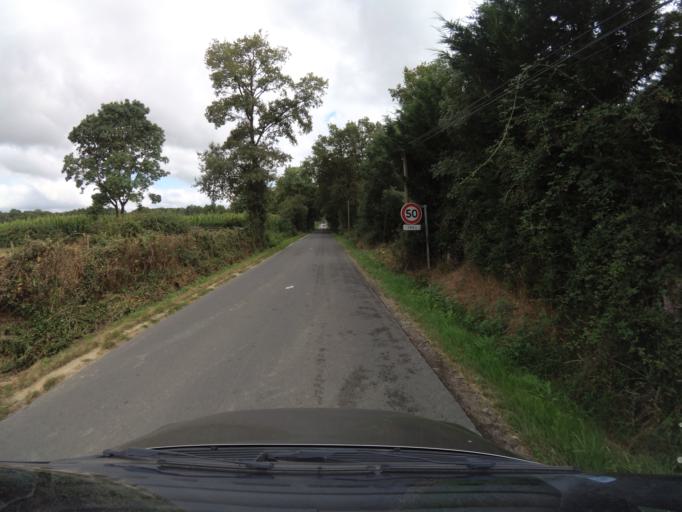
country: FR
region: Pays de la Loire
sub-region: Departement de la Loire-Atlantique
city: La Limouziniere
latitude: 47.0229
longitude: -1.5702
